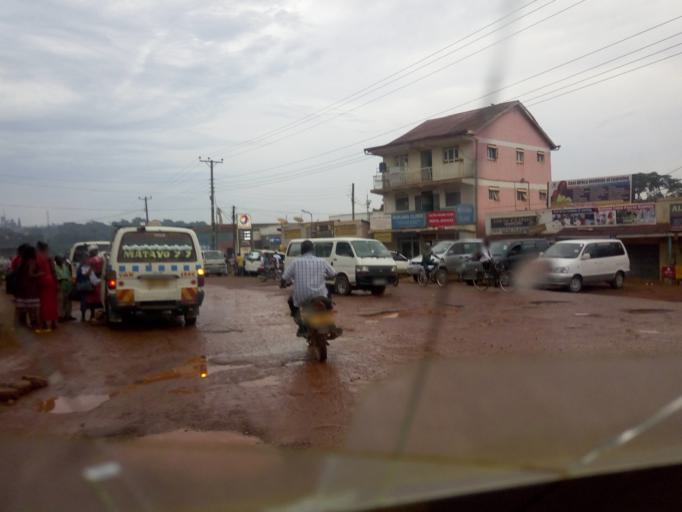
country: UG
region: Central Region
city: Kampala Central Division
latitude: 0.3257
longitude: 32.5582
